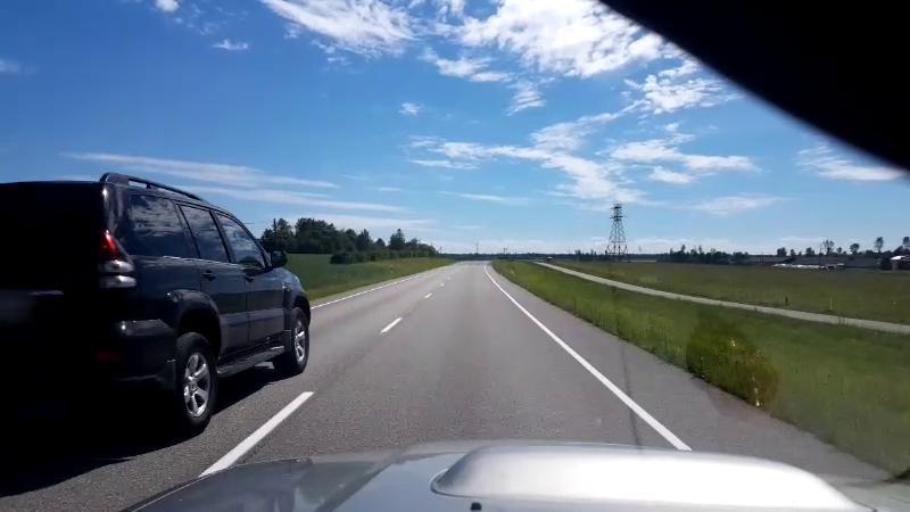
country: EE
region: Jaervamaa
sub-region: Jaerva-Jaani vald
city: Jarva-Jaani
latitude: 59.0272
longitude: 25.8966
